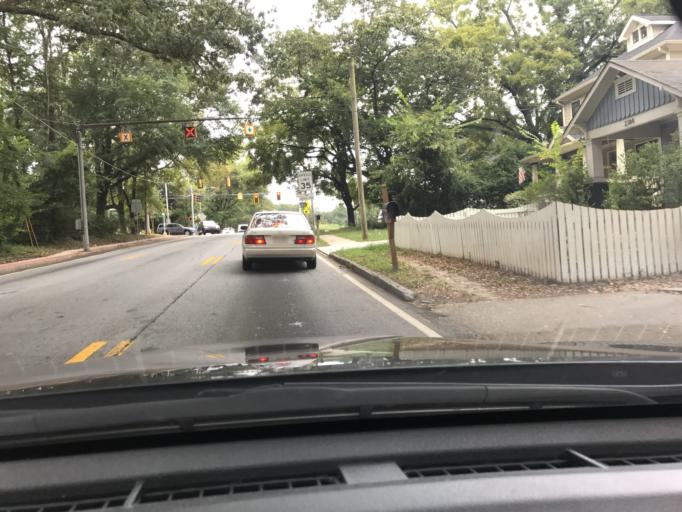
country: US
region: Georgia
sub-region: DeKalb County
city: Decatur
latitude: 33.7473
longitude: -84.3090
